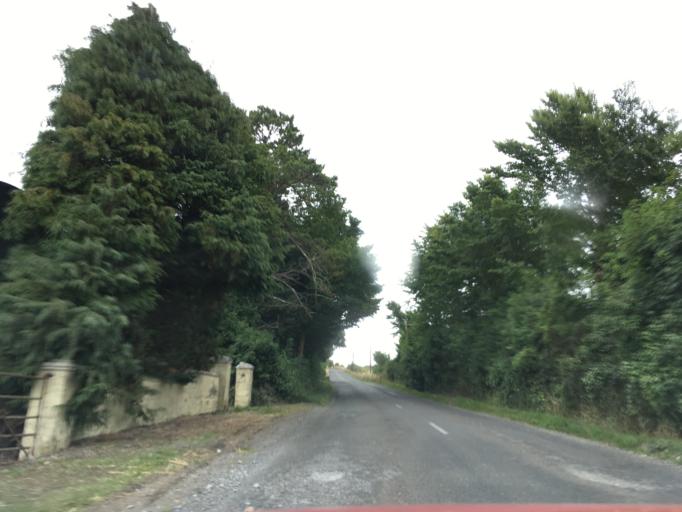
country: IE
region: Munster
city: Cashel
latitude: 52.4682
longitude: -7.8465
